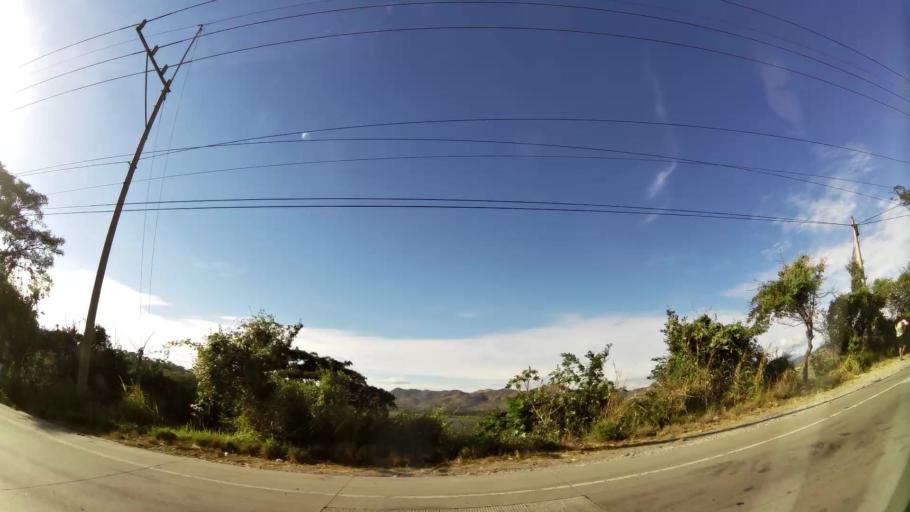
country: SV
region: Santa Ana
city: Metapan
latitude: 14.3011
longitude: -89.4617
